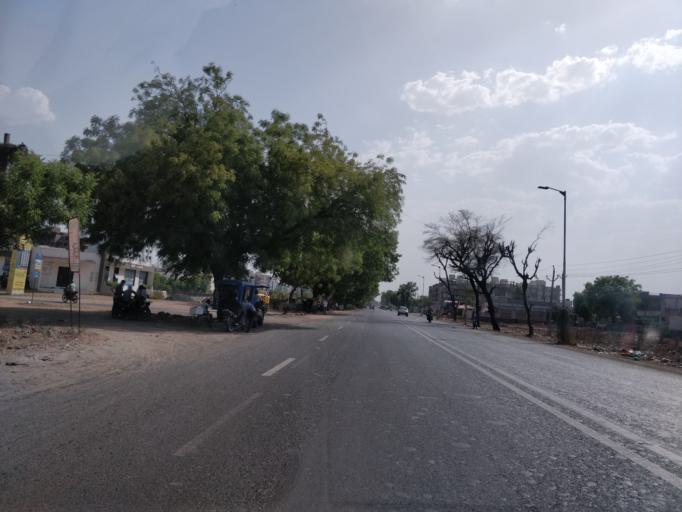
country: IN
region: Gujarat
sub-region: Ahmadabad
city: Naroda
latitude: 23.0833
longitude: 72.6763
